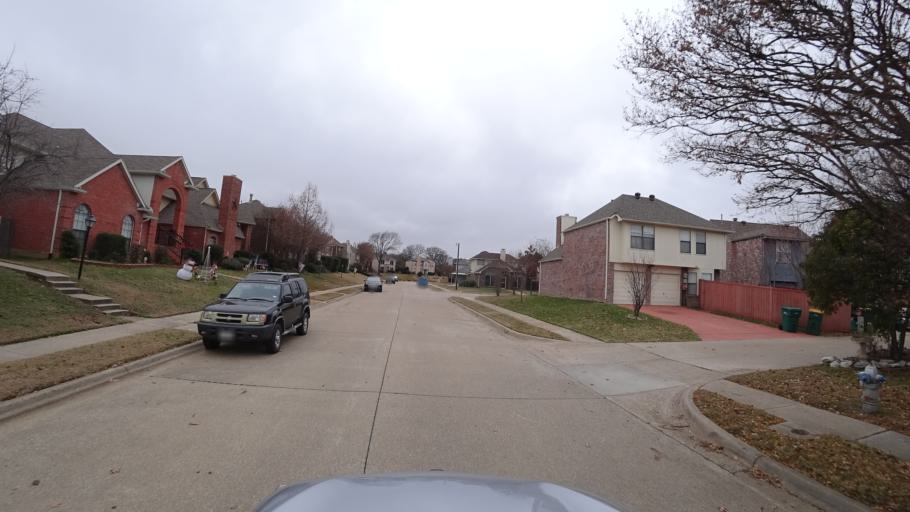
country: US
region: Texas
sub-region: Denton County
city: Lewisville
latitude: 33.0233
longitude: -97.0297
